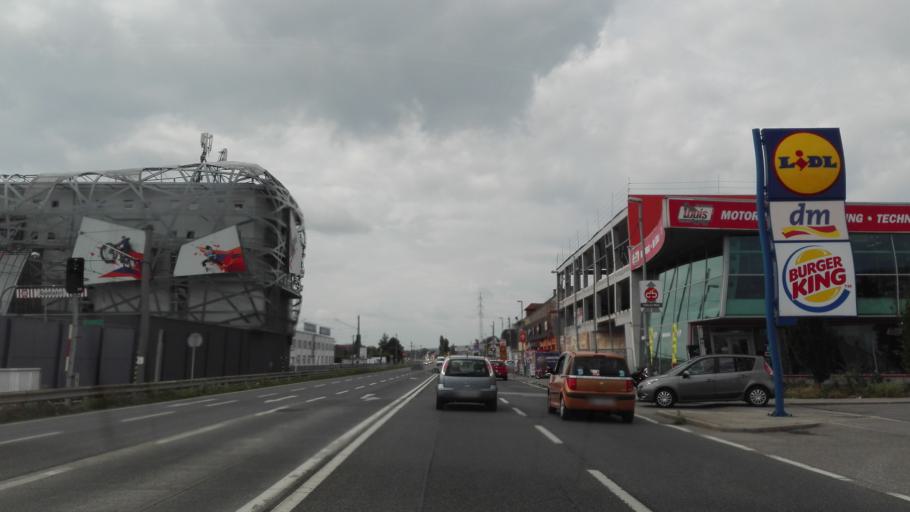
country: AT
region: Lower Austria
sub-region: Politischer Bezirk Modling
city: Vosendorf
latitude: 48.1356
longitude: 16.3247
